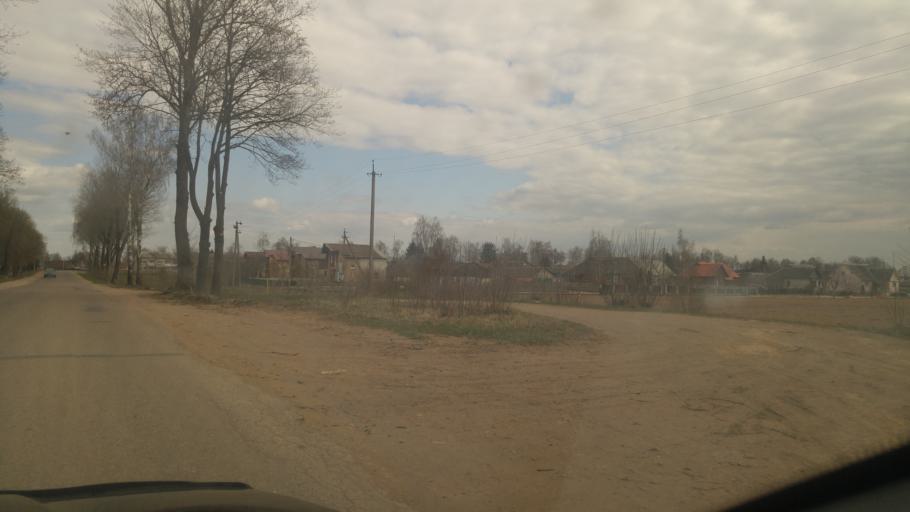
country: BY
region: Minsk
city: Rudzyensk
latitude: 53.6583
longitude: 27.7983
